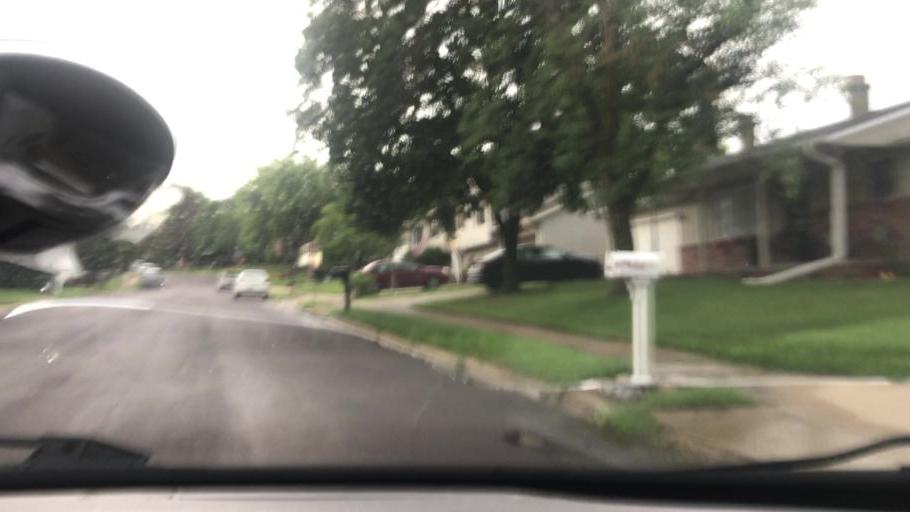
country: US
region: Illinois
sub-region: Tazewell County
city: Pekin
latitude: 40.5420
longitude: -89.6192
